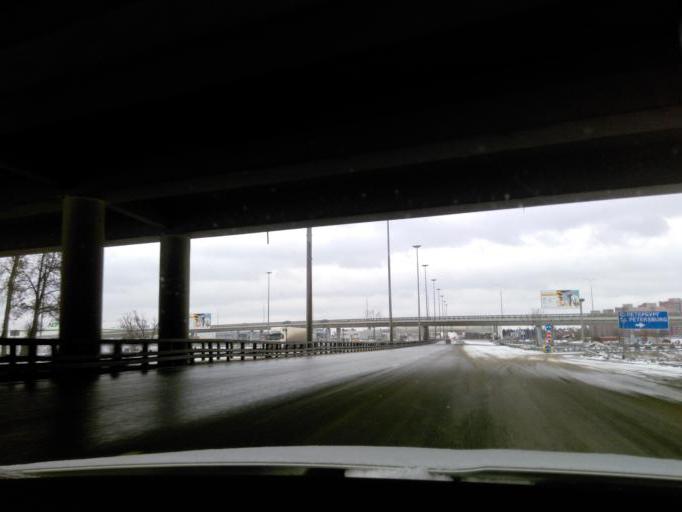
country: RU
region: Moskovskaya
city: Rzhavki
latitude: 56.0006
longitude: 37.2424
